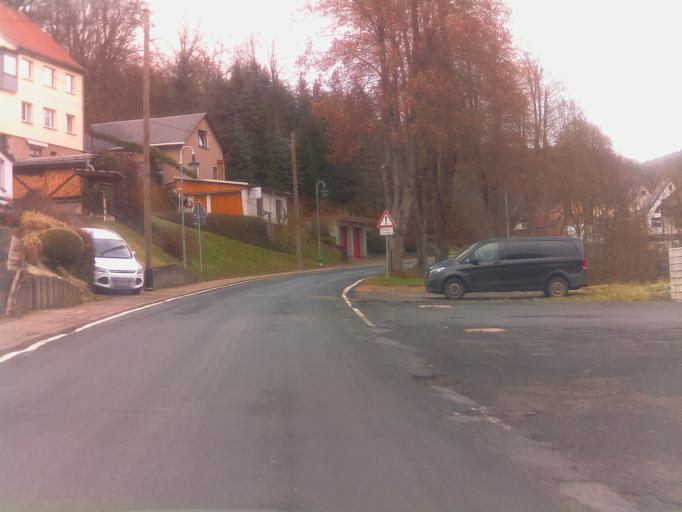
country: DE
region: Thuringia
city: Pappenheim
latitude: 50.7985
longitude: 10.4715
